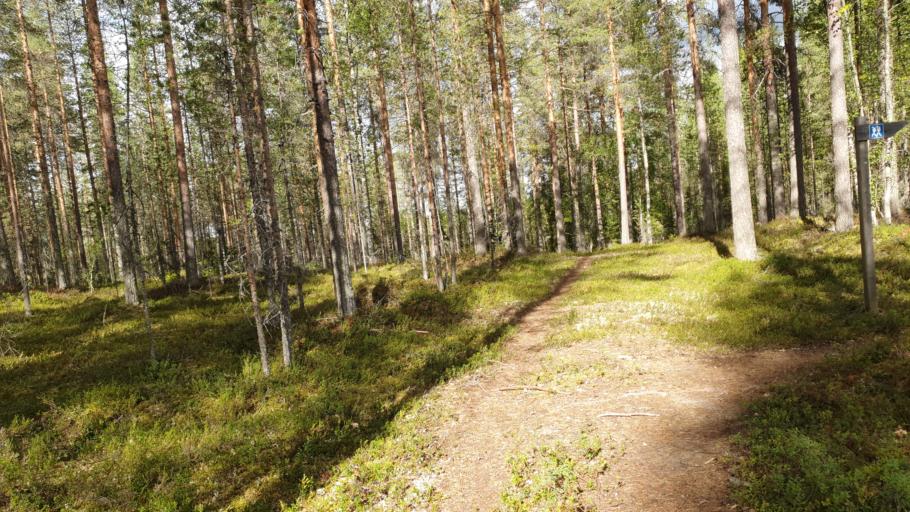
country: FI
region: Kainuu
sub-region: Kehys-Kainuu
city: Kuhmo
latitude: 64.0851
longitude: 29.5270
